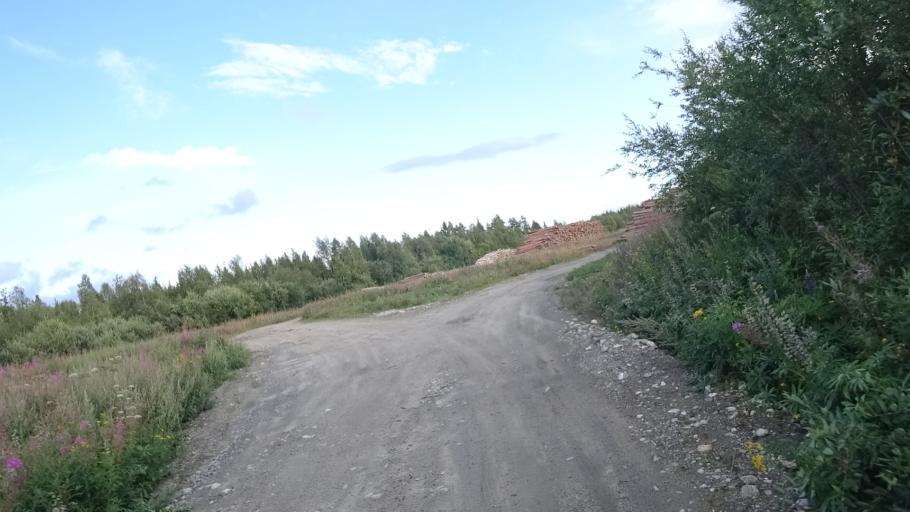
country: FI
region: North Karelia
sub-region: Joensuu
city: Ilomantsi
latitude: 62.6677
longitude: 30.9502
